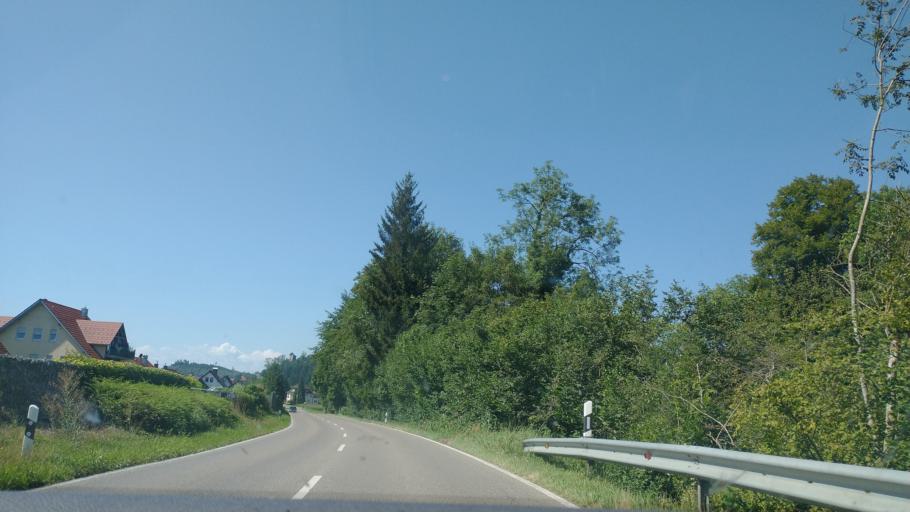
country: DE
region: Bavaria
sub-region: Swabia
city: Hergensweiler
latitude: 47.6463
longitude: 9.7669
